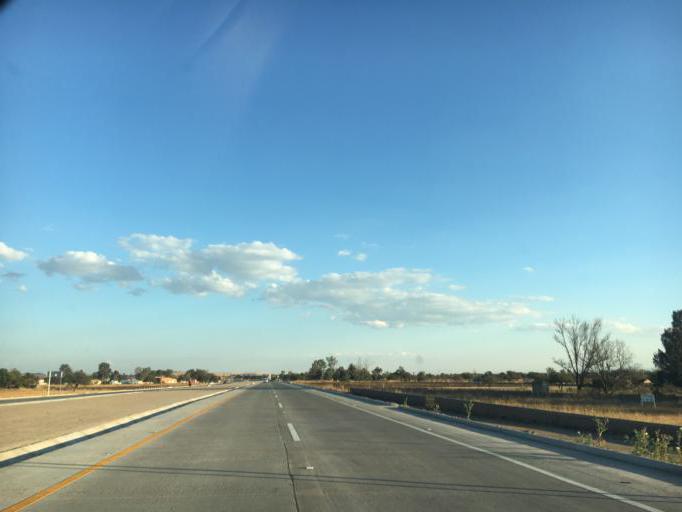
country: MX
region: Guanajuato
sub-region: Leon
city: Ladrilleras del Refugio
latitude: 21.0892
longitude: -101.5597
